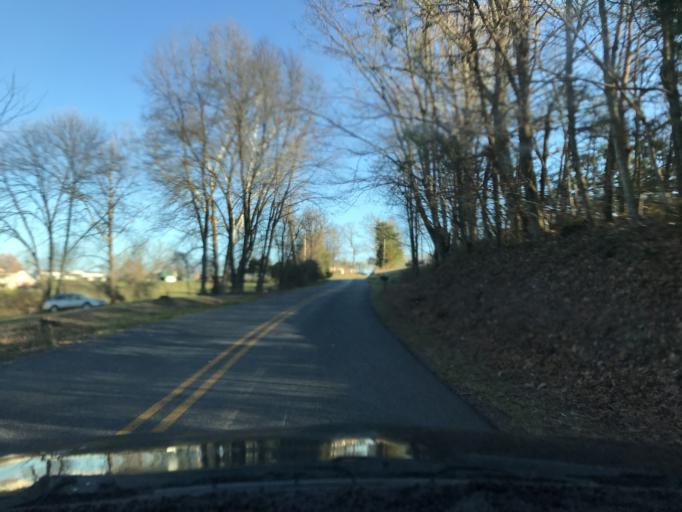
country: US
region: Virginia
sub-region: Botetourt County
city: Blue Ridge
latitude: 37.3970
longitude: -79.7248
